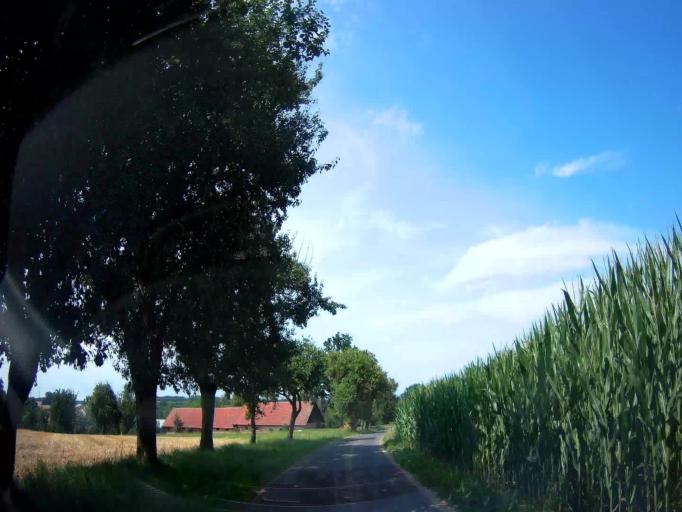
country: AT
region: Upper Austria
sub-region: Politischer Bezirk Kirchdorf an der Krems
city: Kremsmunster
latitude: 48.0761
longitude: 14.0984
